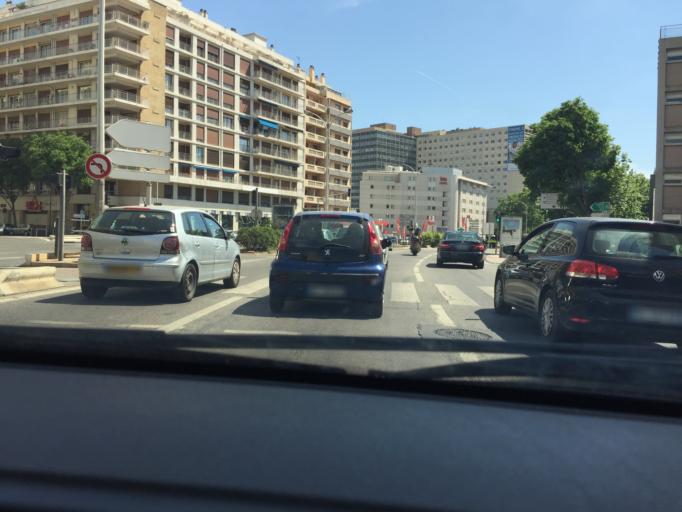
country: FR
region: Provence-Alpes-Cote d'Azur
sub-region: Departement des Bouches-du-Rhone
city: Marseille 05
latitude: 43.2940
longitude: 5.4014
